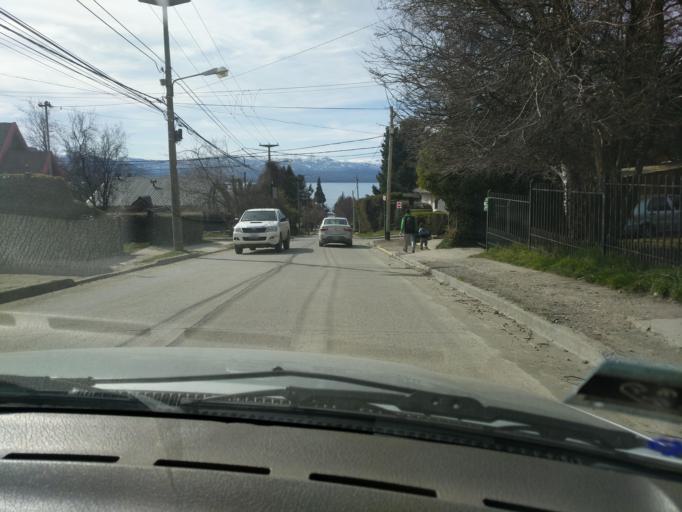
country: AR
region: Rio Negro
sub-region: Departamento de Bariloche
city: San Carlos de Bariloche
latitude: -41.1313
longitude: -71.3567
